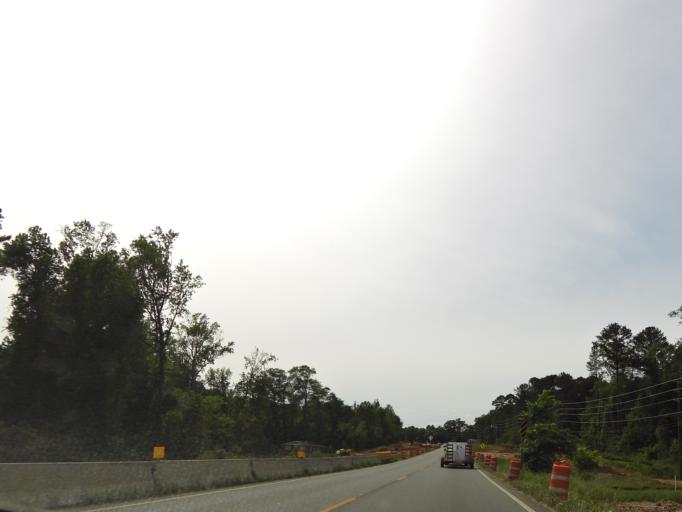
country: US
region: Georgia
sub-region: Houston County
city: Robins Air Force Base
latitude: 32.5522
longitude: -83.6125
